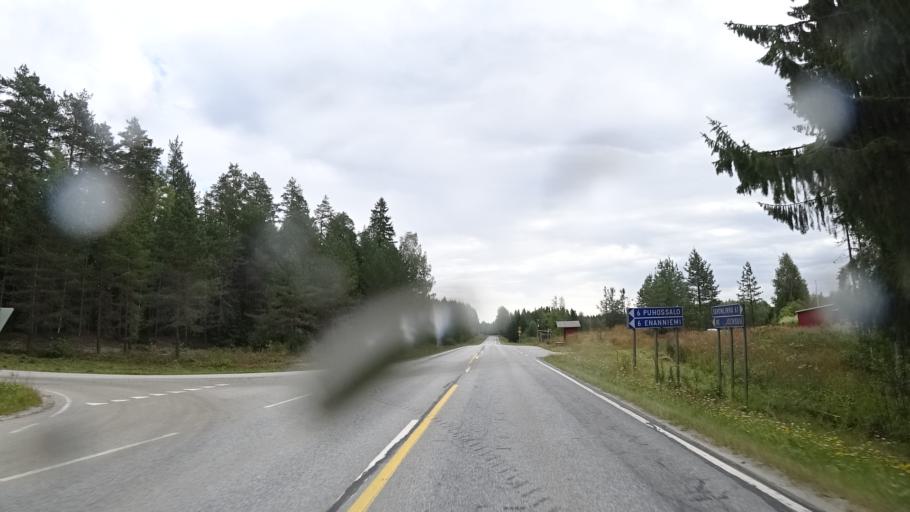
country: FI
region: North Karelia
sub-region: Keski-Karjala
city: Kesaelahti
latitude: 62.1103
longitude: 29.7389
